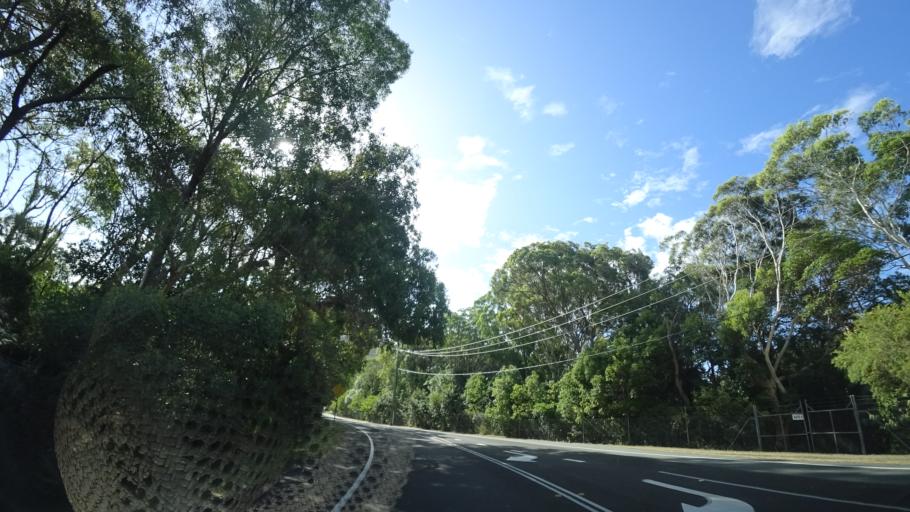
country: AU
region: Queensland
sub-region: Sunshine Coast
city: Coolum Beach
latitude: -26.5620
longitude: 153.0938
